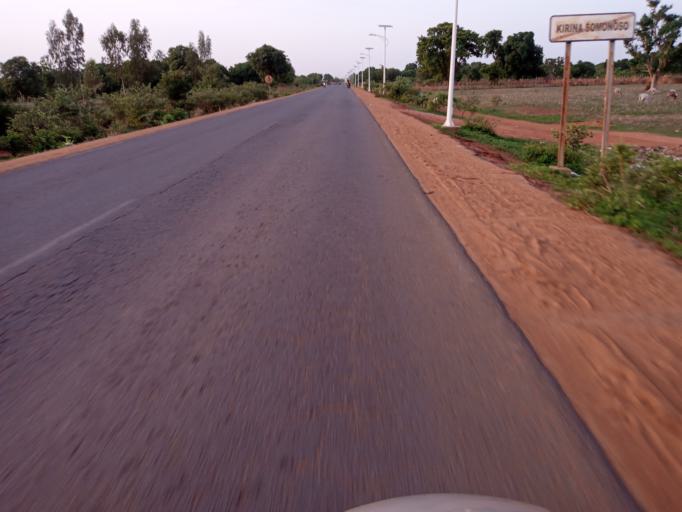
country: ML
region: Bamako
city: Bamako
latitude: 12.3012
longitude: -8.1582
